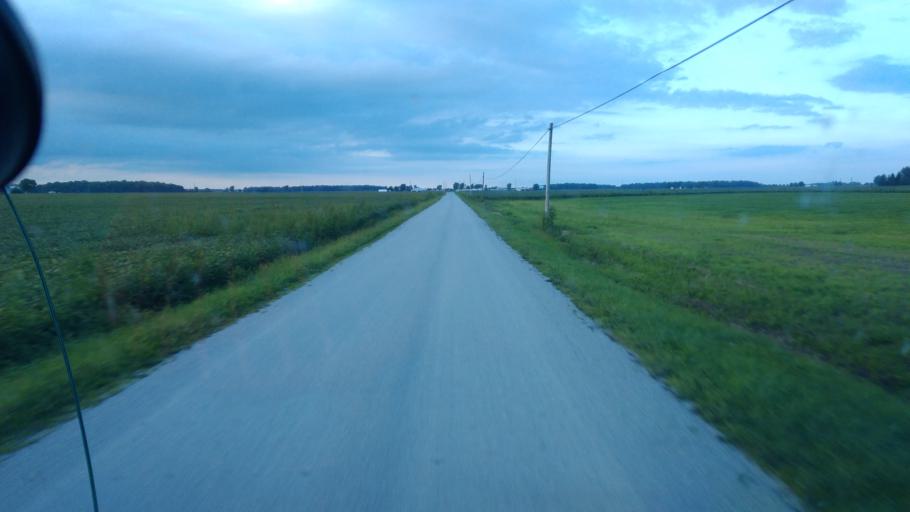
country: US
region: Ohio
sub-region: Hardin County
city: Kenton
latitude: 40.6673
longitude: -83.5145
